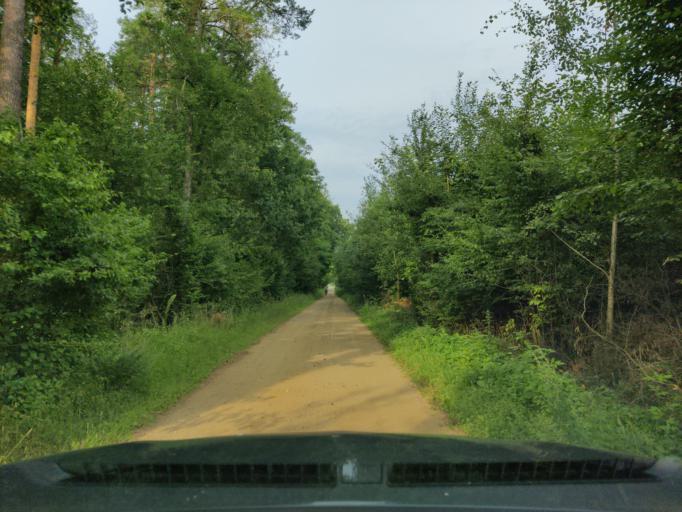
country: PL
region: Masovian Voivodeship
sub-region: Powiat pultuski
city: Obryte
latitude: 52.7039
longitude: 21.2225
